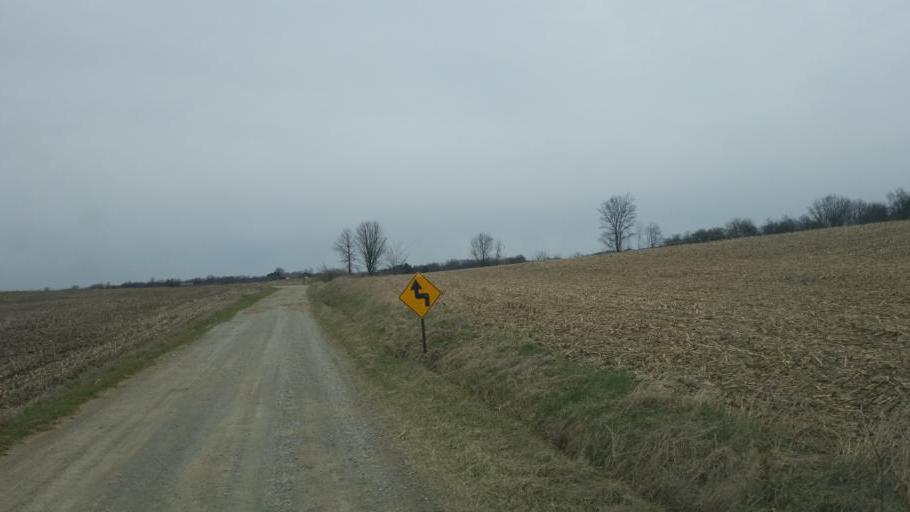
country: US
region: Ohio
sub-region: Knox County
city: Centerburg
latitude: 40.3083
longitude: -82.6687
